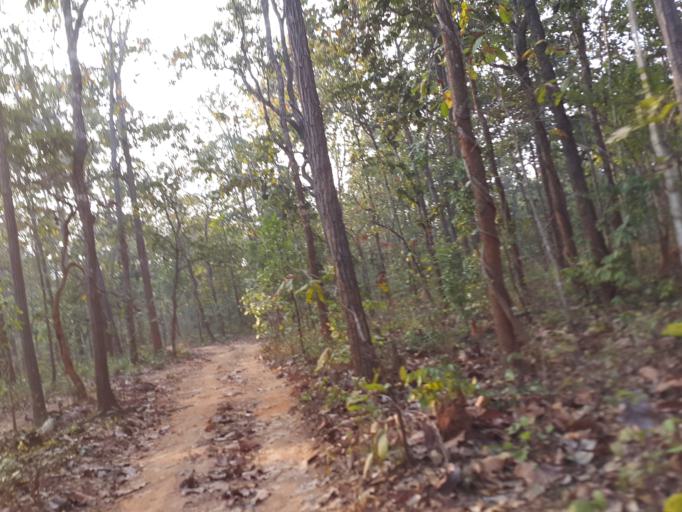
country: TH
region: Lamphun
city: Li
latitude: 17.6131
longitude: 98.8882
